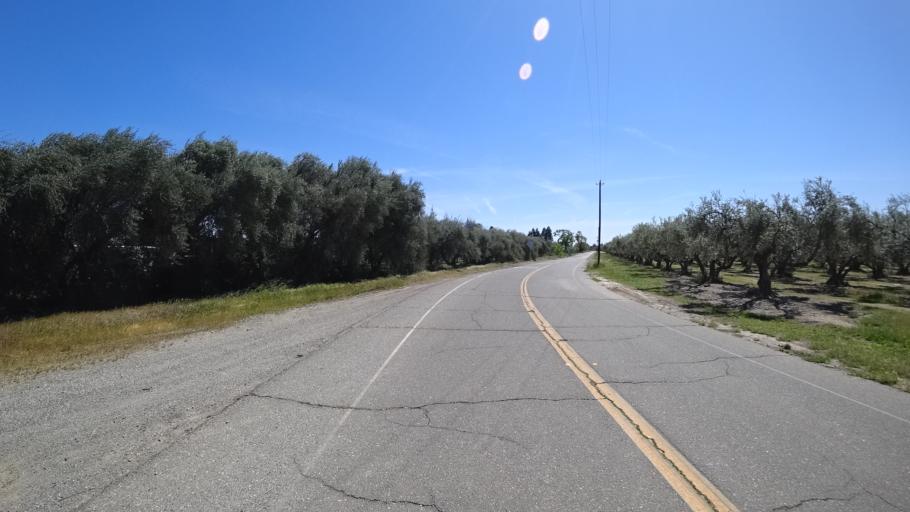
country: US
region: California
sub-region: Glenn County
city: Orland
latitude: 39.7460
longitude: -122.1596
